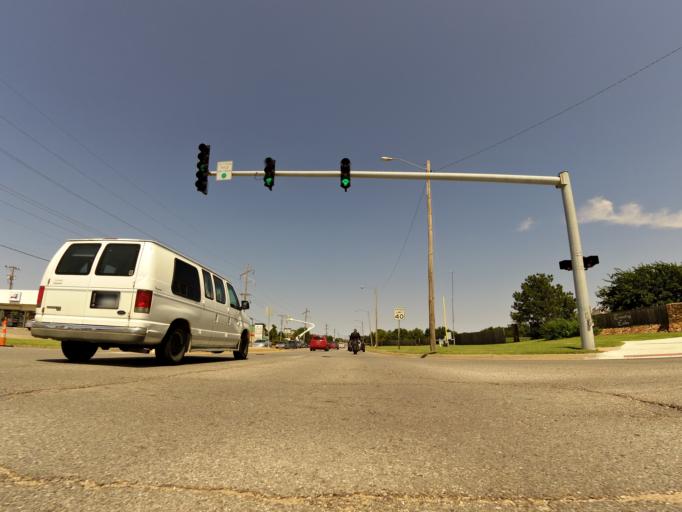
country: US
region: Kansas
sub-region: Sedgwick County
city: Bellaire
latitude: 37.7230
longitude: -97.2623
